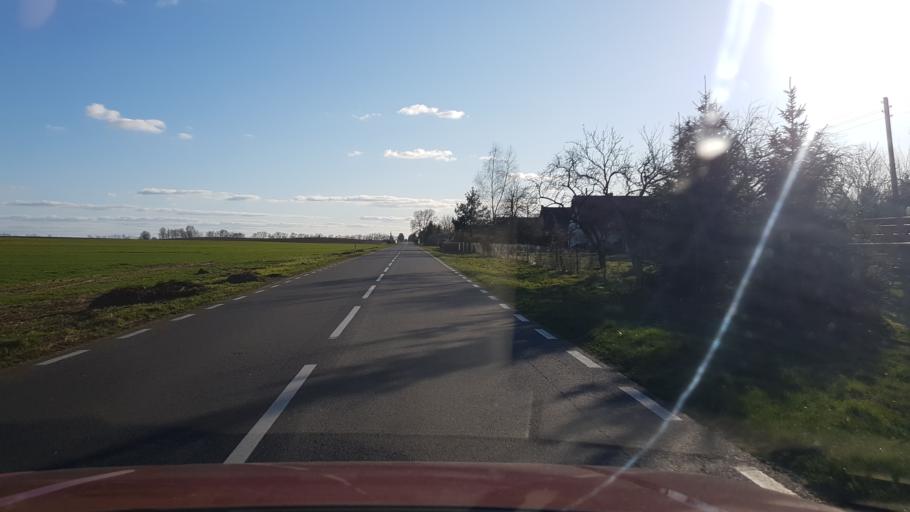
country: PL
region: West Pomeranian Voivodeship
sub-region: Powiat stargardzki
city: Stargard Szczecinski
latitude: 53.3740
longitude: 15.0775
